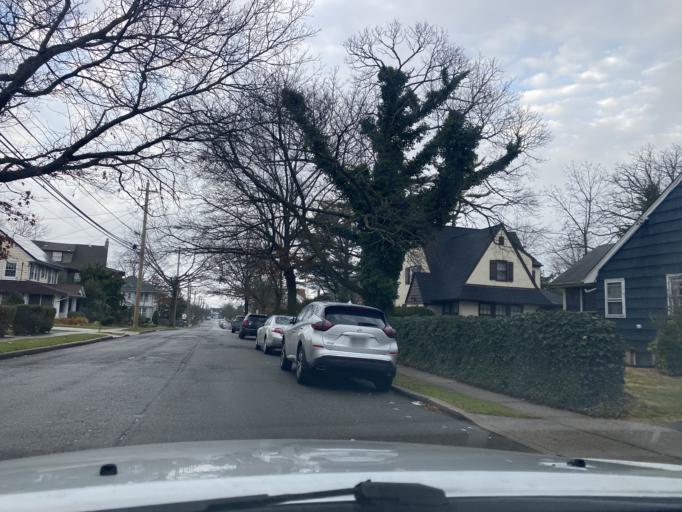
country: US
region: New York
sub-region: Nassau County
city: Cedarhurst
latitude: 40.6223
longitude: -73.7282
